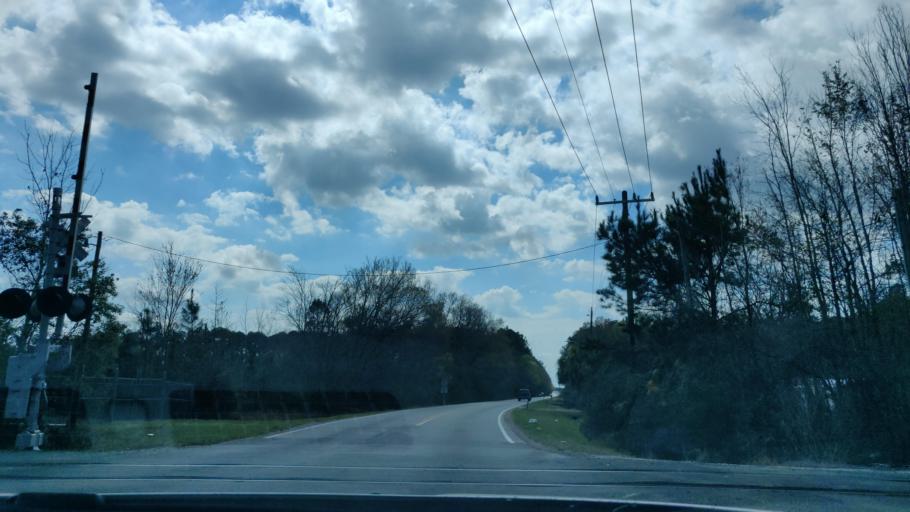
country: US
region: Florida
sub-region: Duval County
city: Baldwin
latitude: 30.3014
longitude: -81.9666
